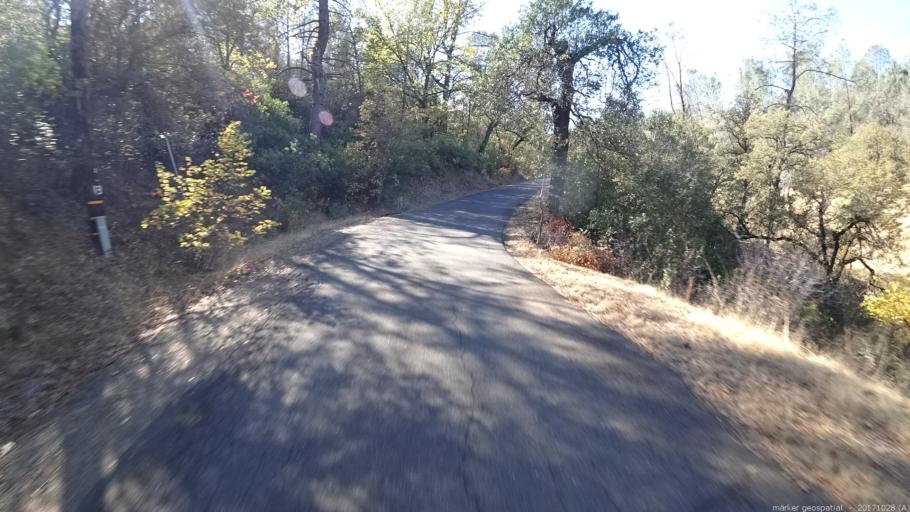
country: US
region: California
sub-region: Shasta County
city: Shasta
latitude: 40.5955
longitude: -122.4510
